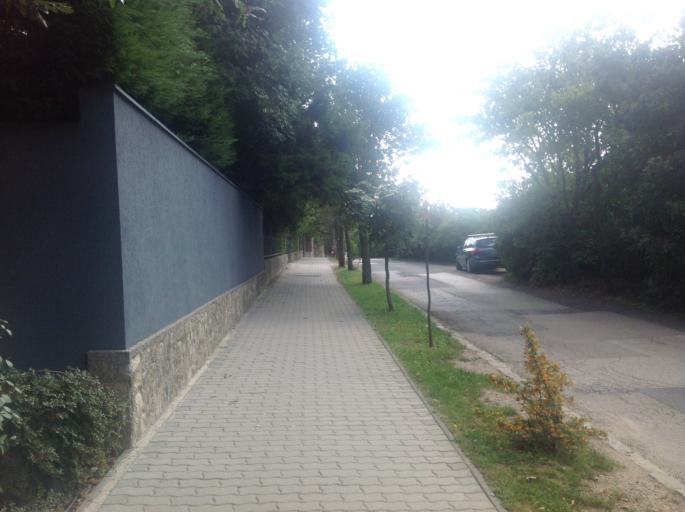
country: HU
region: Pest
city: Budaors
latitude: 47.4983
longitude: 18.9728
